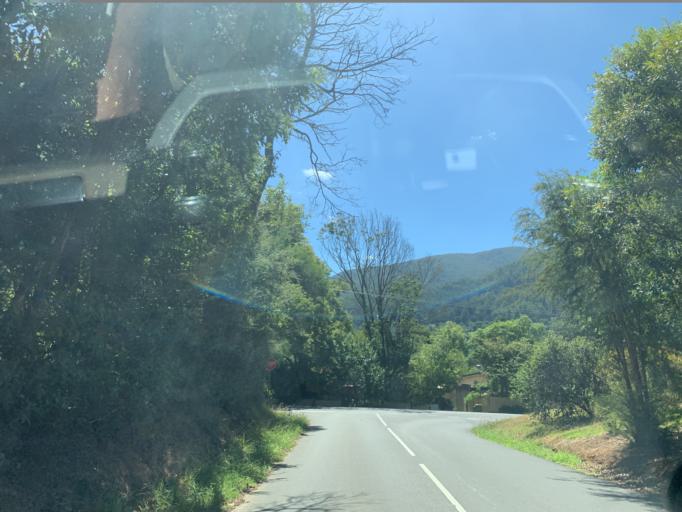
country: AU
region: Victoria
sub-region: Yarra Ranges
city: Millgrove
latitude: -37.7553
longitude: 145.6973
